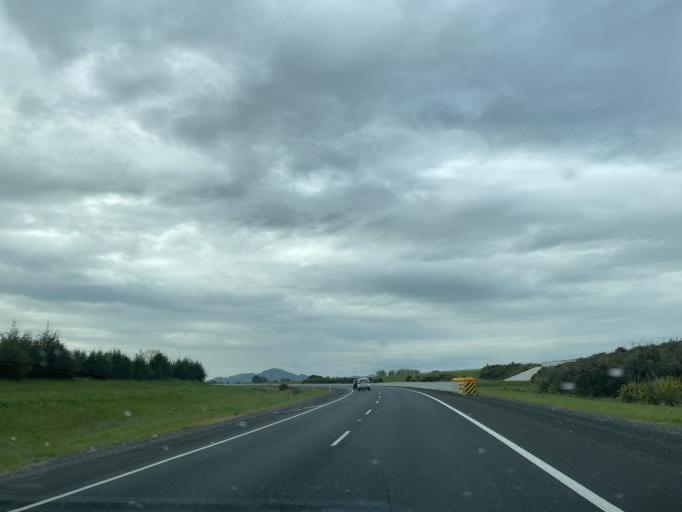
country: NZ
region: Waikato
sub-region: Waikato District
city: Ngaruawahia
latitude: -37.6856
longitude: 175.2155
